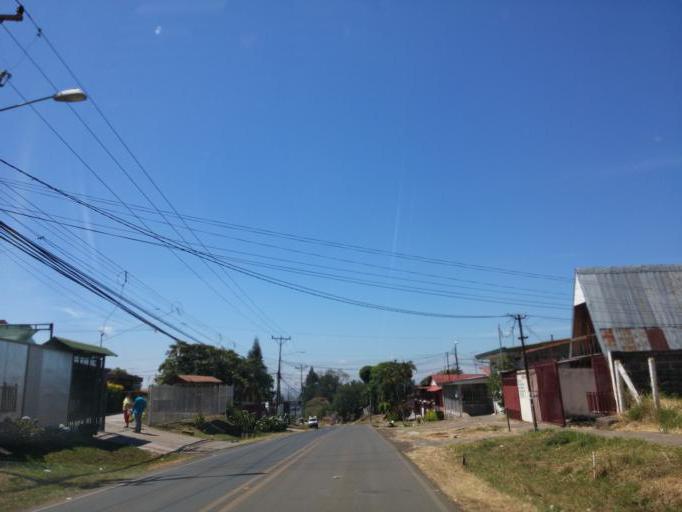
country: CR
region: Alajuela
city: Alajuela
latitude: 10.0359
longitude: -84.2115
